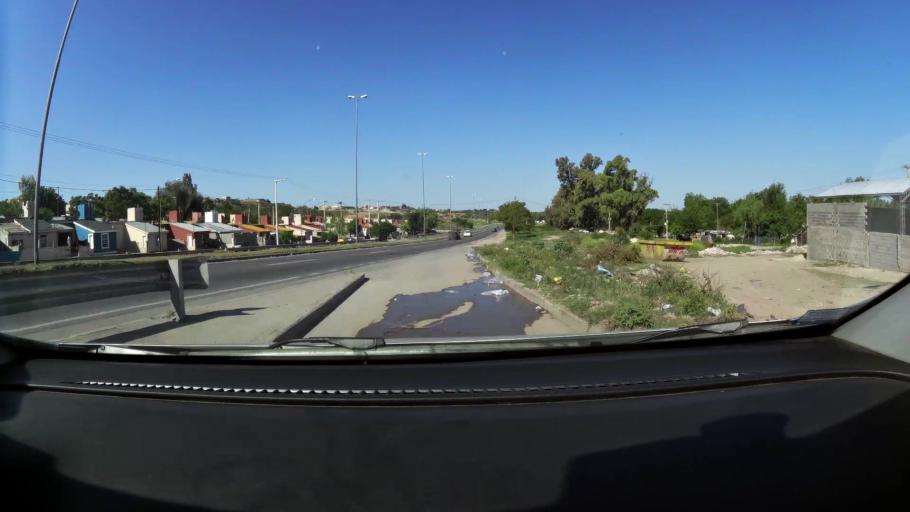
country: AR
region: Cordoba
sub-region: Departamento de Capital
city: Cordoba
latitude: -31.4013
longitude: -64.1491
